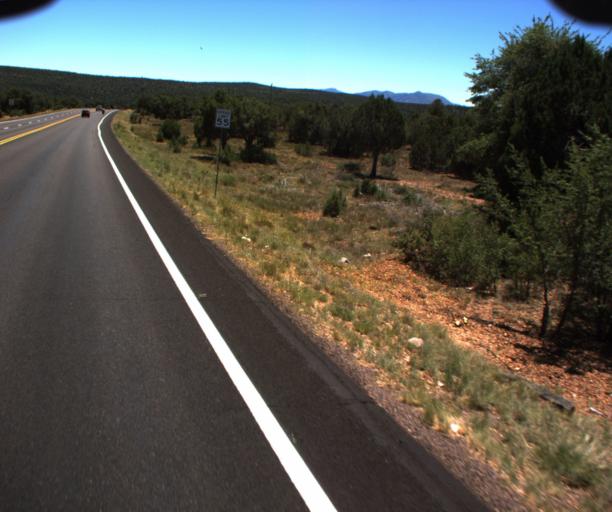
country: US
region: Arizona
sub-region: Gila County
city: Pine
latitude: 34.3295
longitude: -111.4187
